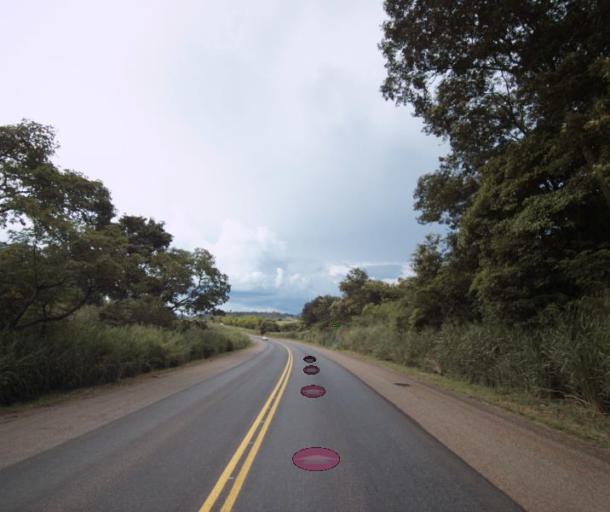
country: BR
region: Goias
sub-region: Ceres
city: Ceres
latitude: -15.2057
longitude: -49.5453
